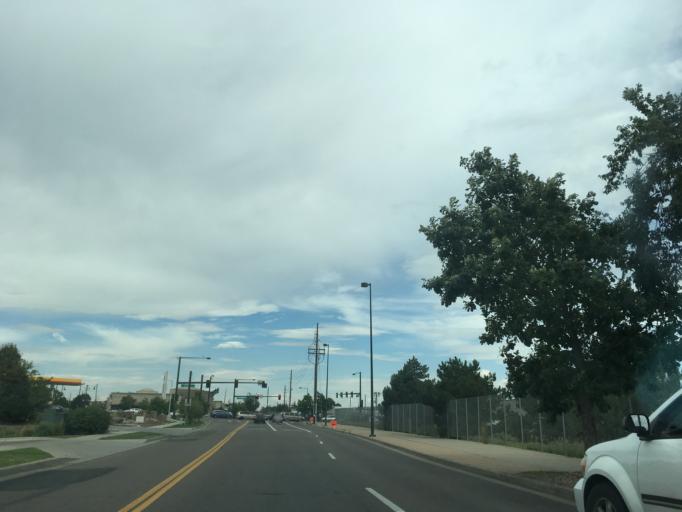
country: US
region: Colorado
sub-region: Arapahoe County
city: Englewood
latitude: 39.6894
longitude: -104.9941
